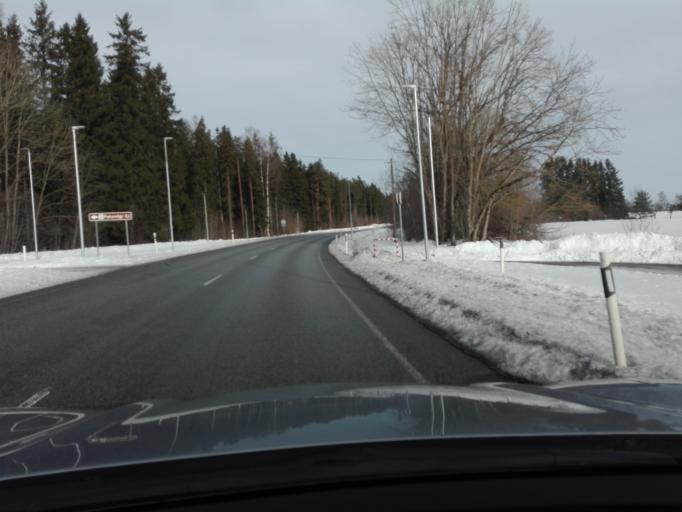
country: EE
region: Raplamaa
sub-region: Rapla vald
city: Rapla
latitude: 58.9384
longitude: 24.7474
